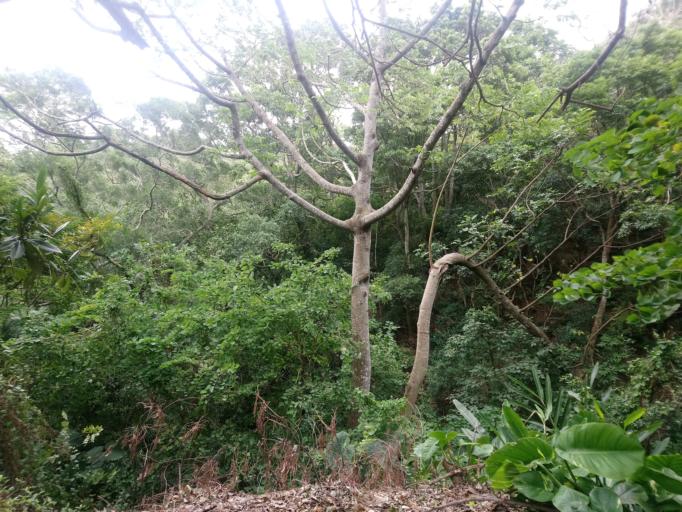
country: TW
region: Taiwan
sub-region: Hsinchu
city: Hsinchu
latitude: 24.7923
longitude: 120.9860
